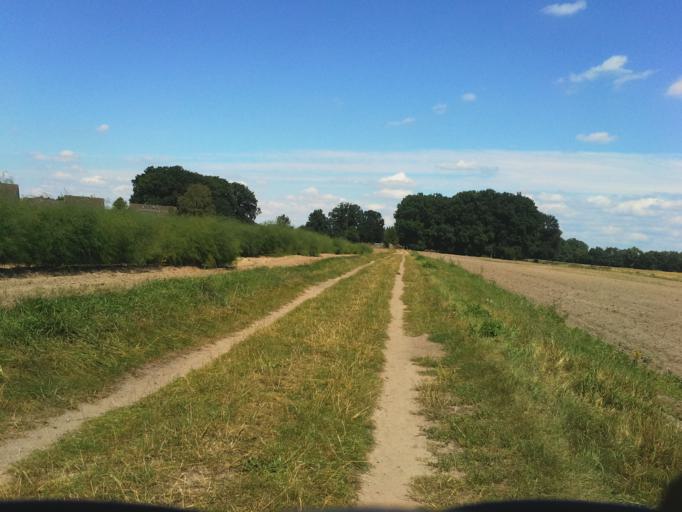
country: DE
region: Lower Saxony
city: Nienburg
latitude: 52.6551
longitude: 9.2395
